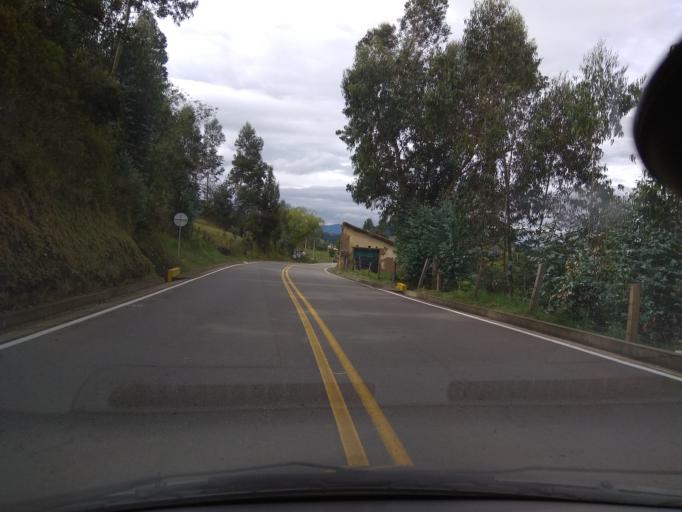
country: CO
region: Boyaca
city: Santa Rosa de Viterbo
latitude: 5.8969
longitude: -72.9762
